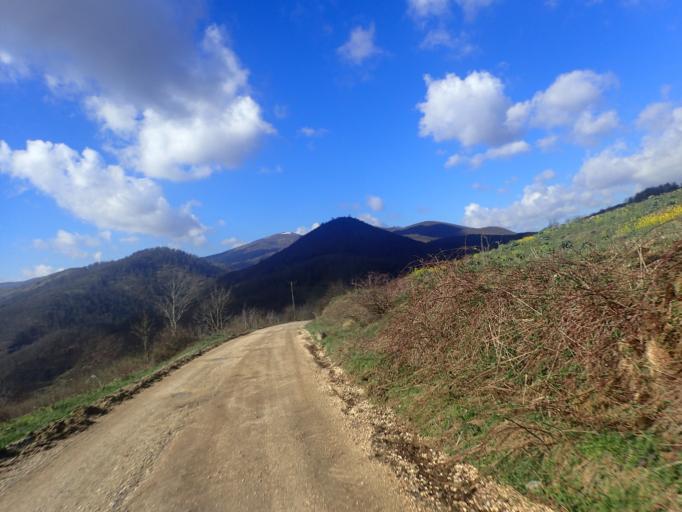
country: TR
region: Ordu
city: Kumru
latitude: 40.8075
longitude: 37.1850
